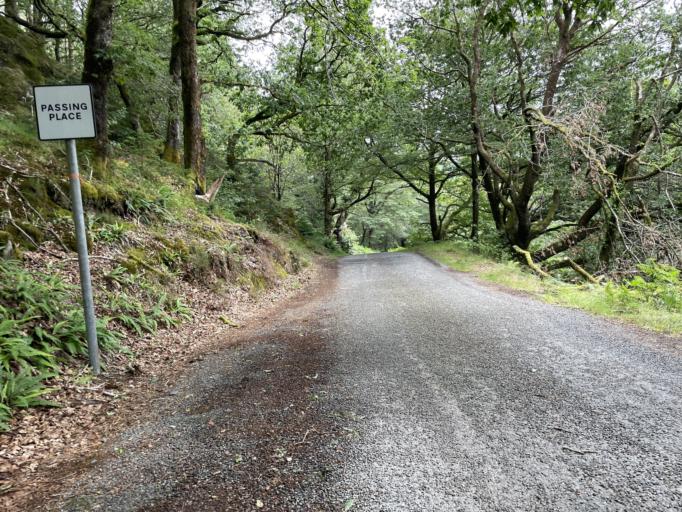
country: GB
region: Scotland
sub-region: Dumfries and Galloway
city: Newton Stewart
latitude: 55.0905
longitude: -4.4942
